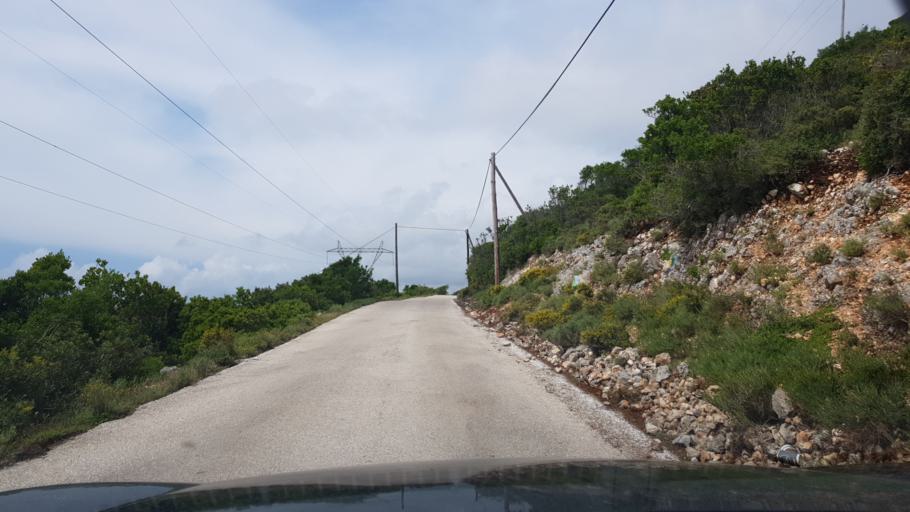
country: GR
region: Ionian Islands
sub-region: Lefkada
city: Nidri
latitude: 38.6049
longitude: 20.5606
